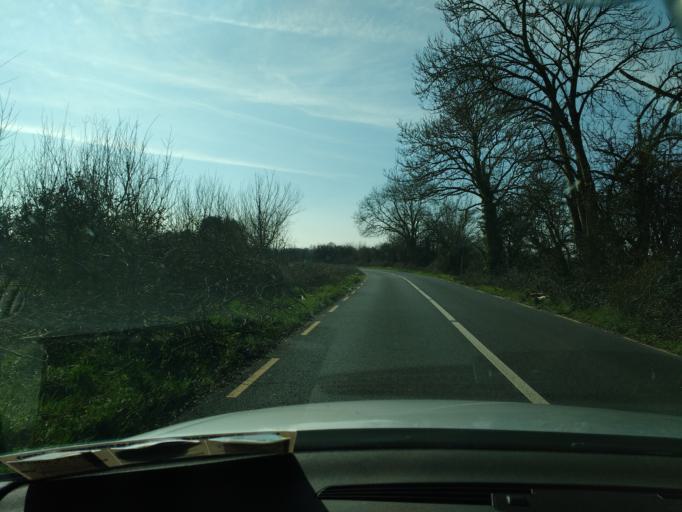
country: IE
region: Munster
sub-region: County Limerick
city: Castleconnell
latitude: 52.7009
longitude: -8.4593
